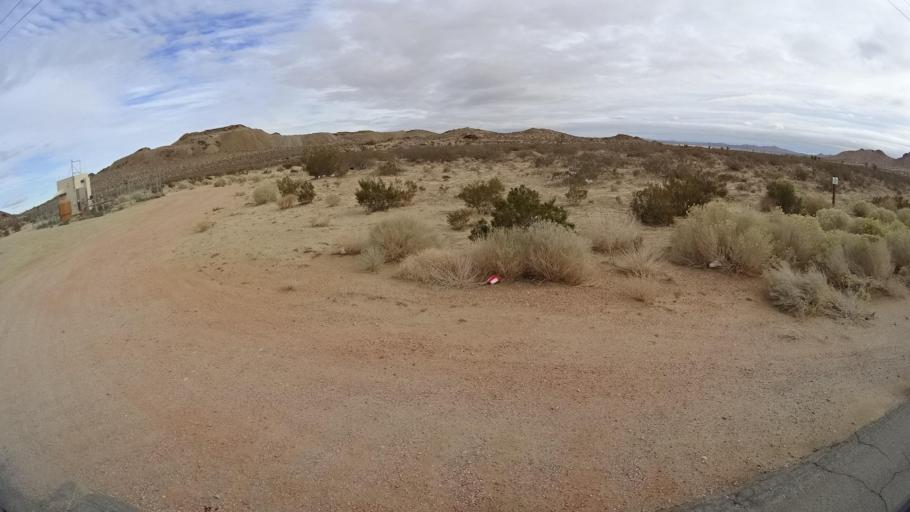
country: US
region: California
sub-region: Kern County
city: Mojave
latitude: 35.0014
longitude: -118.1865
